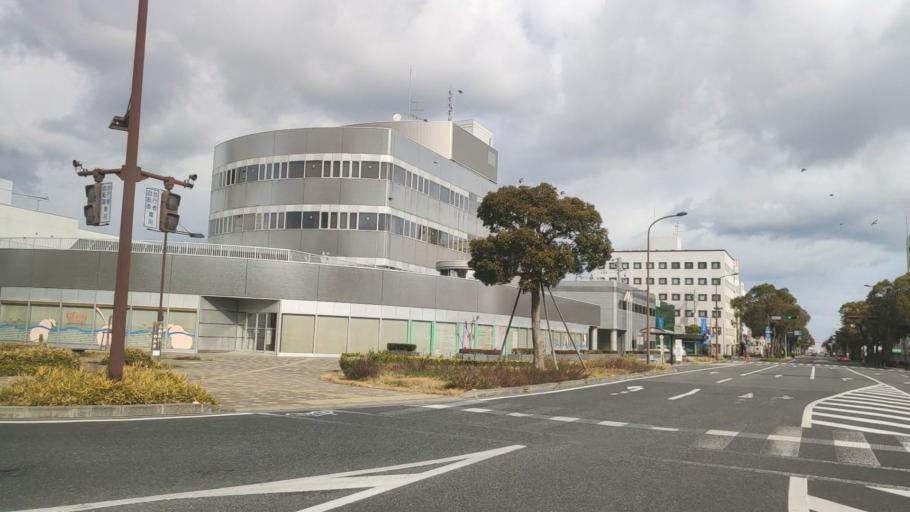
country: JP
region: Ehime
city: Saijo
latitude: 34.0667
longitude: 132.9985
